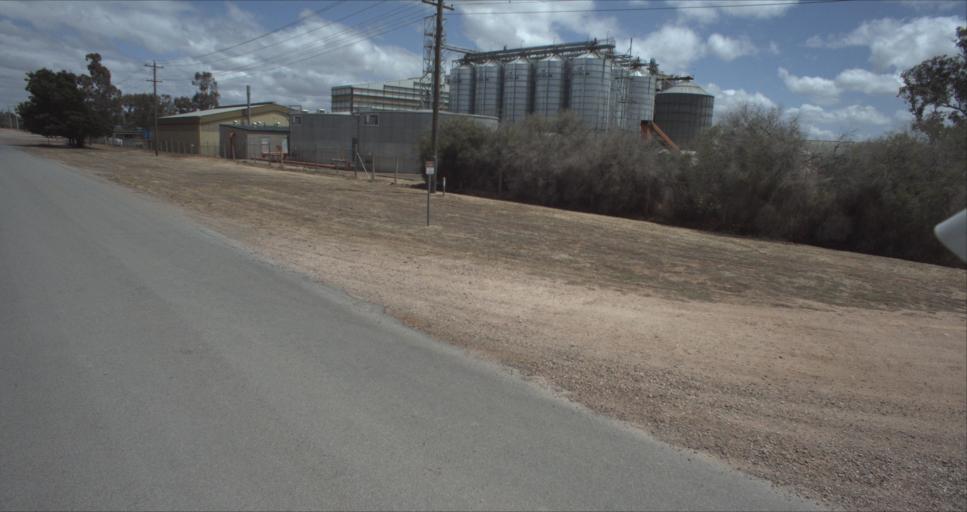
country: AU
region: New South Wales
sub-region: Leeton
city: Leeton
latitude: -34.5568
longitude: 146.3972
